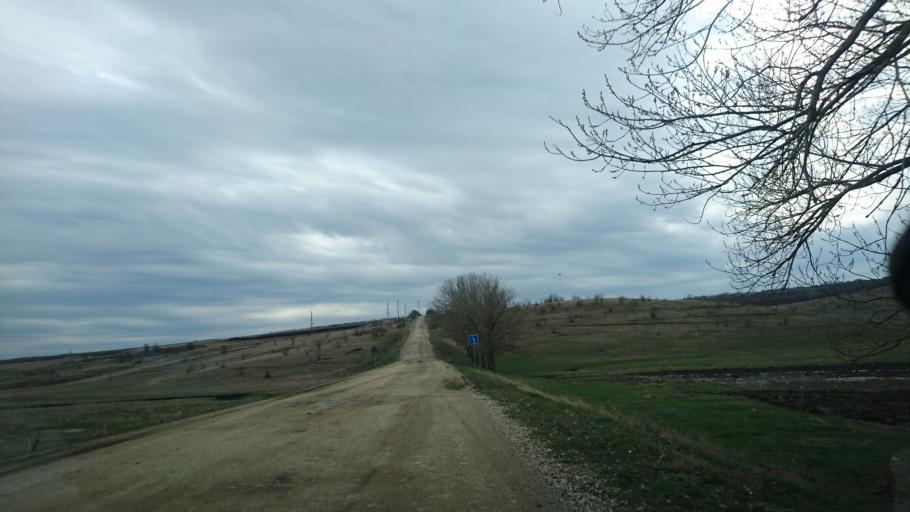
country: MD
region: Cantemir
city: Visniovca
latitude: 46.3124
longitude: 28.4063
